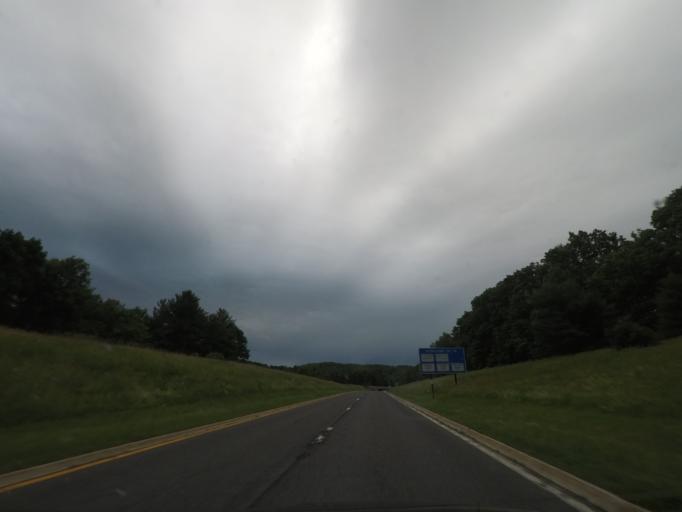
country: US
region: New York
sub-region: Columbia County
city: Chatham
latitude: 42.3501
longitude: -73.5773
